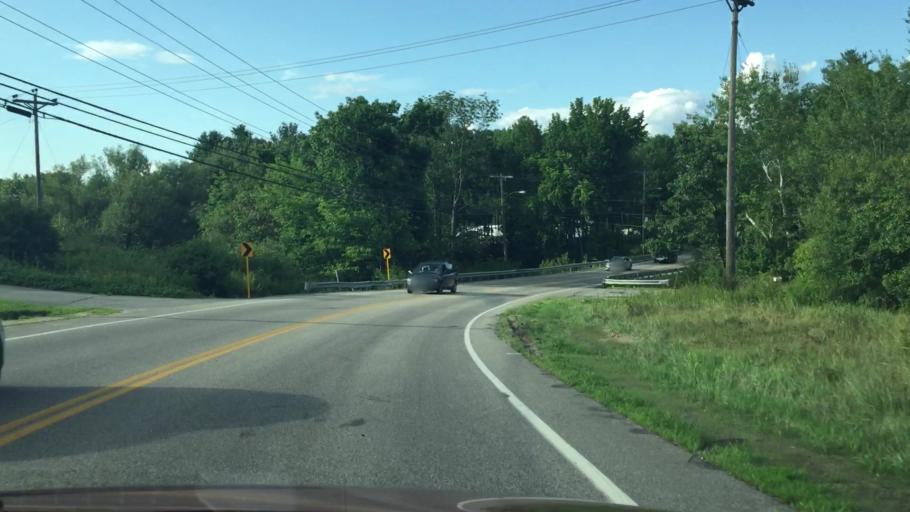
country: US
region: Maine
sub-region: Cumberland County
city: Westbrook
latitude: 43.6598
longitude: -70.3619
